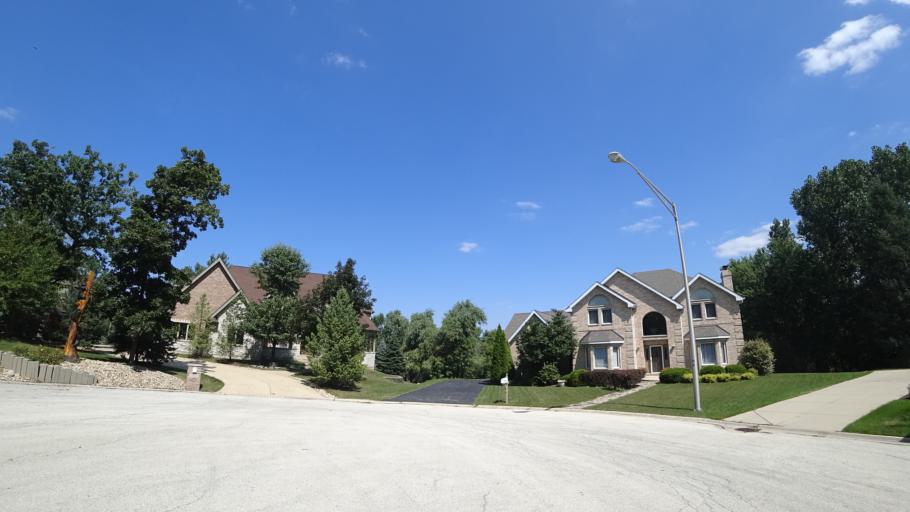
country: US
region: Illinois
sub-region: Cook County
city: Orland Park
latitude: 41.6295
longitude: -87.8424
